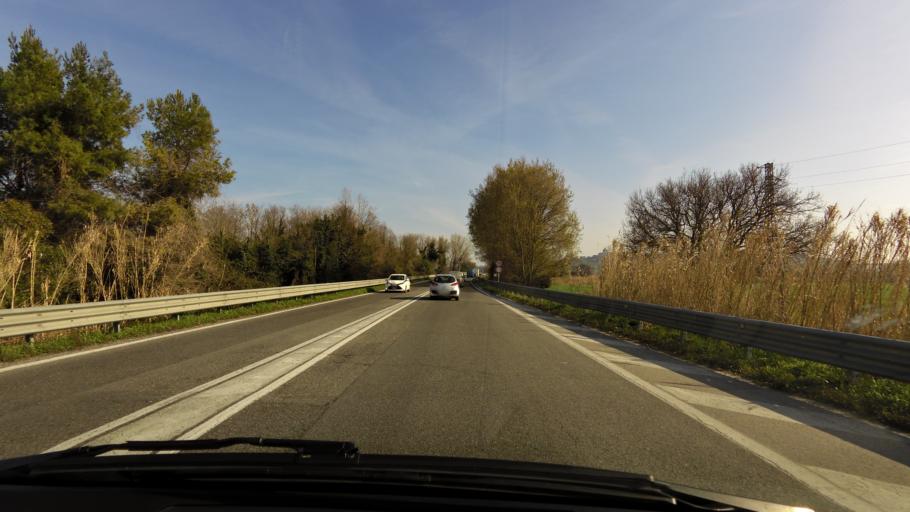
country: IT
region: The Marches
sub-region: Provincia di Ancona
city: Villa Musone
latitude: 43.4644
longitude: 13.6034
